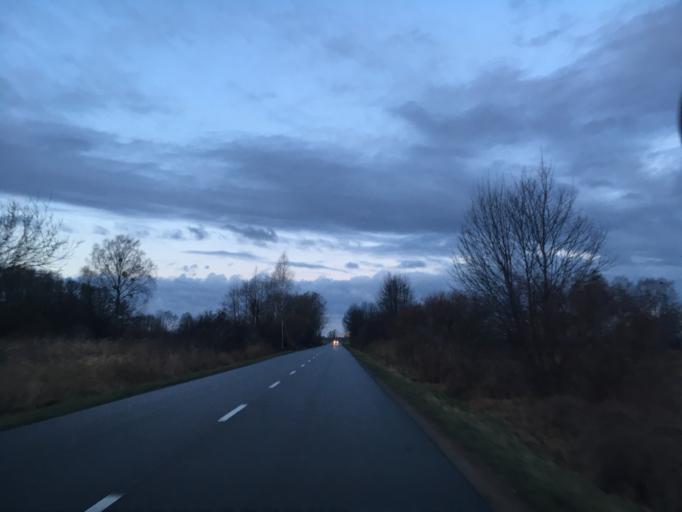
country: PL
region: Masovian Voivodeship
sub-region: Powiat grodziski
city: Podkowa Lesna
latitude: 52.0801
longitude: 20.7370
